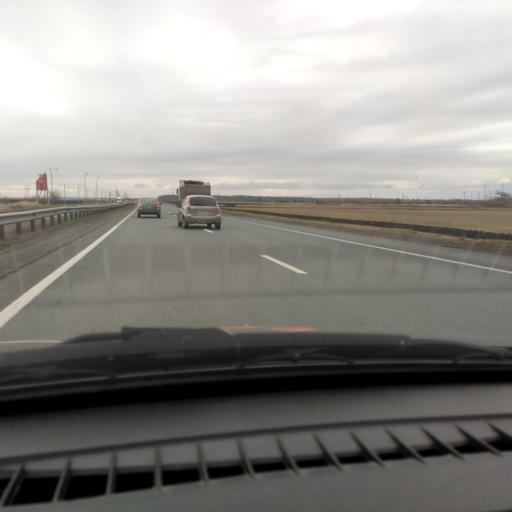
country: RU
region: Samara
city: Zhigulevsk
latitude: 53.5555
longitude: 49.5032
